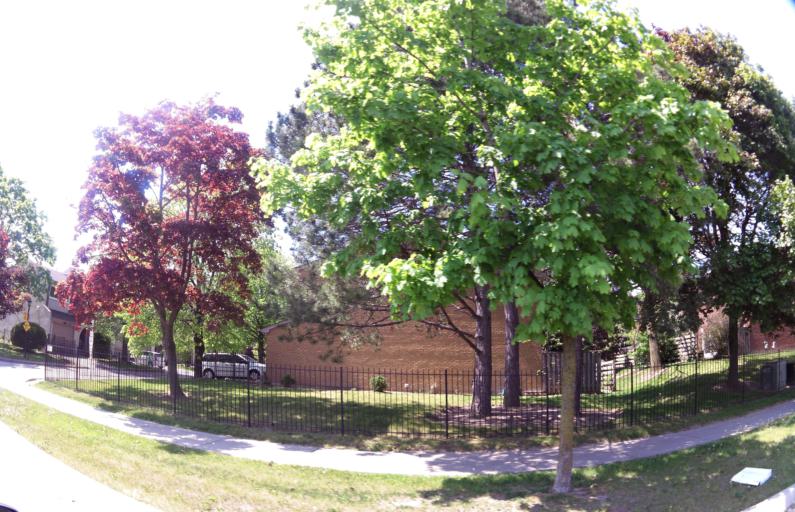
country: CA
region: Ontario
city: Mississauga
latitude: 43.5998
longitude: -79.6230
